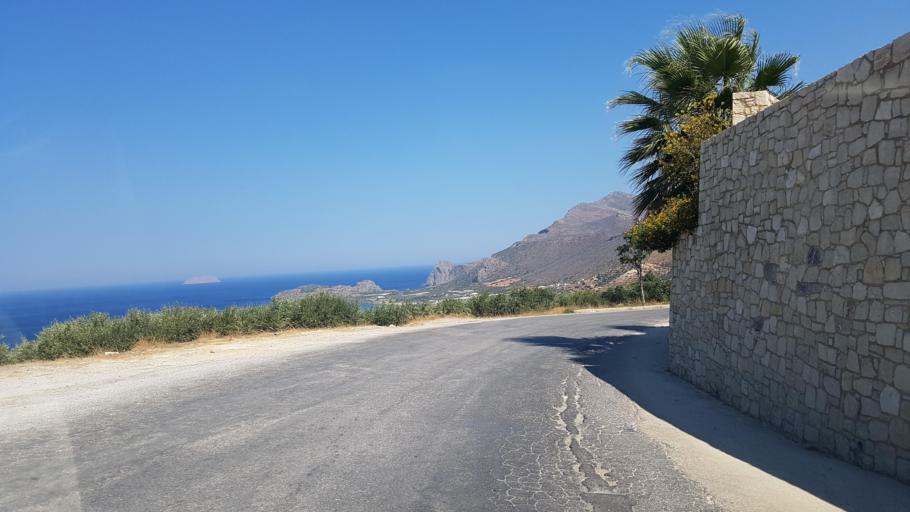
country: GR
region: Crete
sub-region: Nomos Chanias
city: Platanos
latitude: 35.4789
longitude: 23.5920
